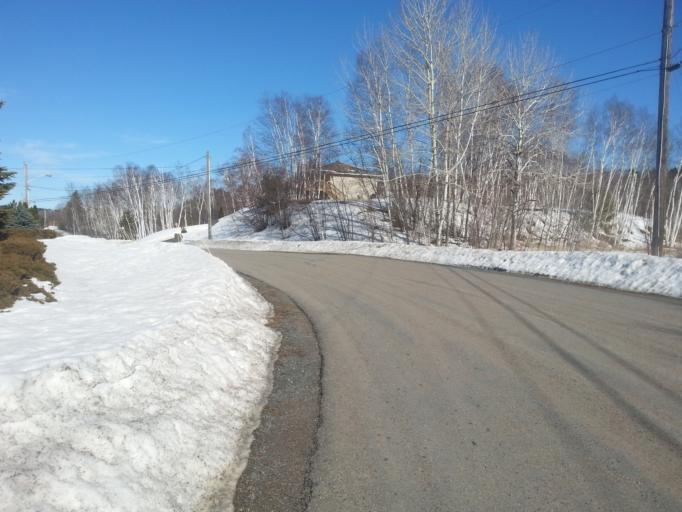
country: CA
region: Ontario
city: Greater Sudbury
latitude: 46.4022
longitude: -81.0330
